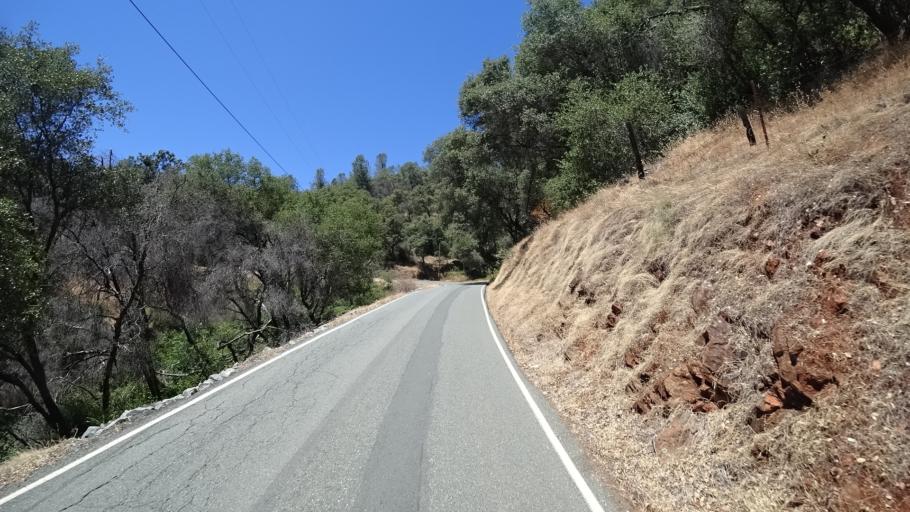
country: US
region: California
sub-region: Calaveras County
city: San Andreas
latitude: 38.2969
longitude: -120.6762
